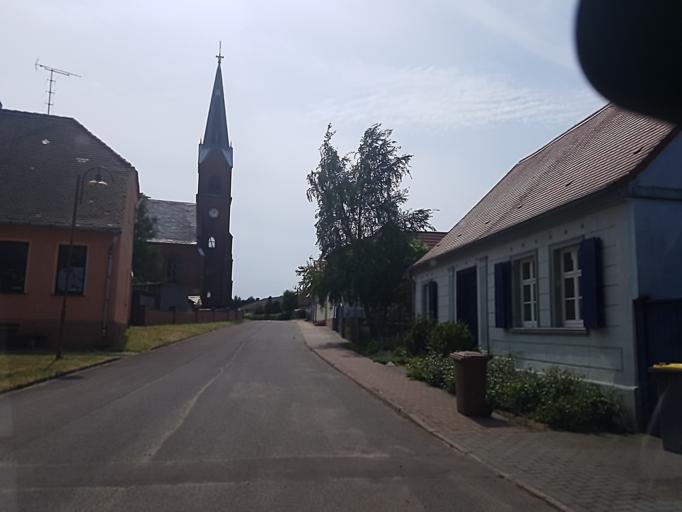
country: DE
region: Brandenburg
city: Gorzke
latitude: 52.0724
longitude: 12.3074
